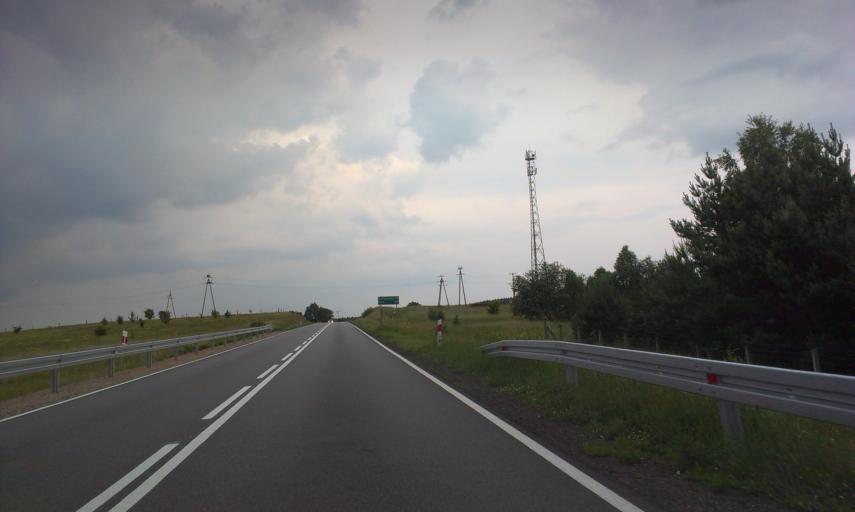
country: PL
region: West Pomeranian Voivodeship
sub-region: Powiat koszalinski
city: Bobolice
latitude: 53.8550
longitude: 16.6117
